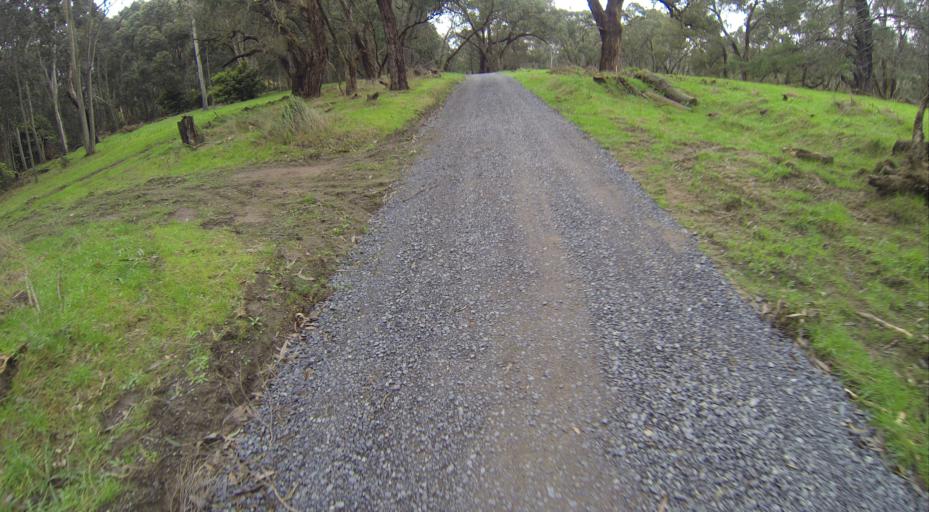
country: AU
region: Victoria
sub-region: Yarra Ranges
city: Lysterfield
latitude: -37.9365
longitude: 145.3122
